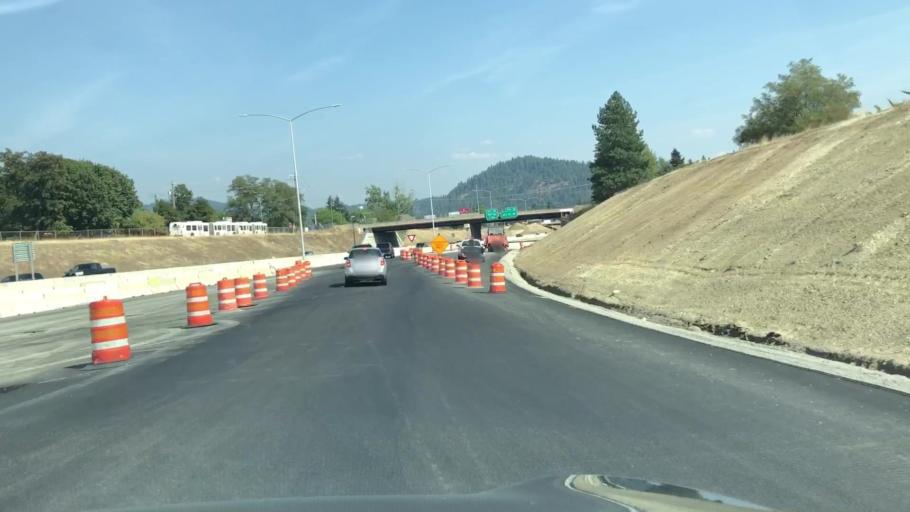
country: US
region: Idaho
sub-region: Kootenai County
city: Coeur d'Alene
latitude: 47.6983
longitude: -116.7892
